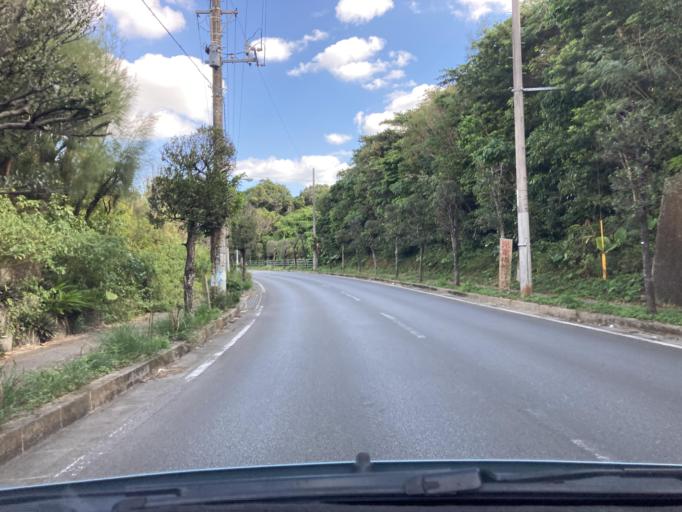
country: JP
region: Okinawa
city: Okinawa
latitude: 26.3430
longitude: 127.8015
